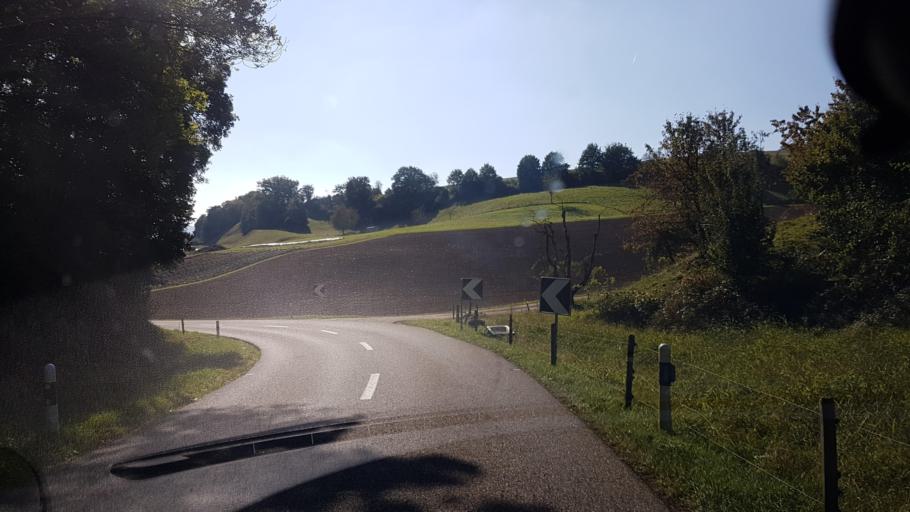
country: CH
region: Aargau
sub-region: Bezirk Laufenburg
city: Sulz
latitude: 47.5138
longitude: 8.1015
